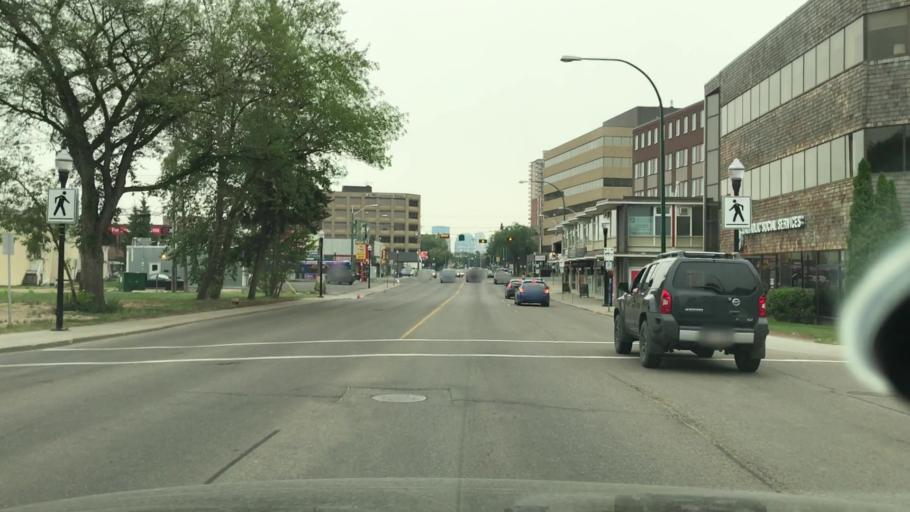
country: CA
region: Alberta
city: Edmonton
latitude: 53.5472
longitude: -113.5379
